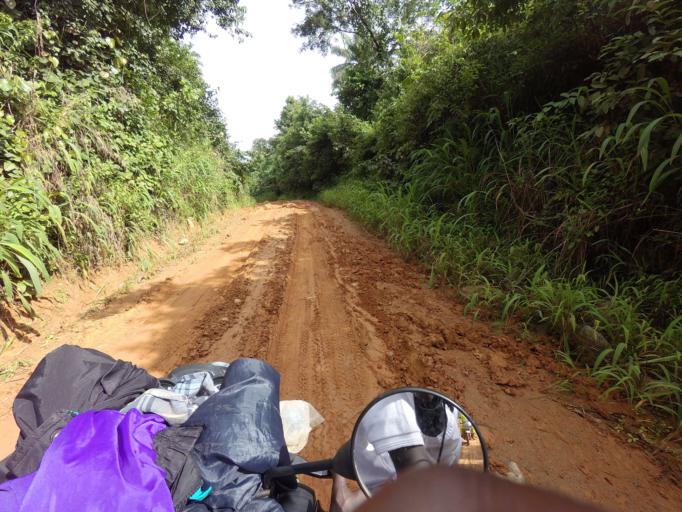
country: SL
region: Eastern Province
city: Tombodu
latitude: 8.1689
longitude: -10.6564
